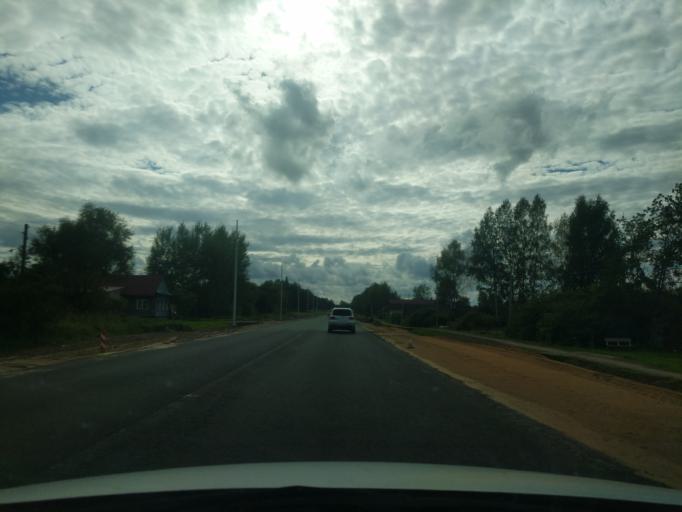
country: RU
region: Jaroslavl
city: Levashevo
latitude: 57.6518
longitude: 40.5539
